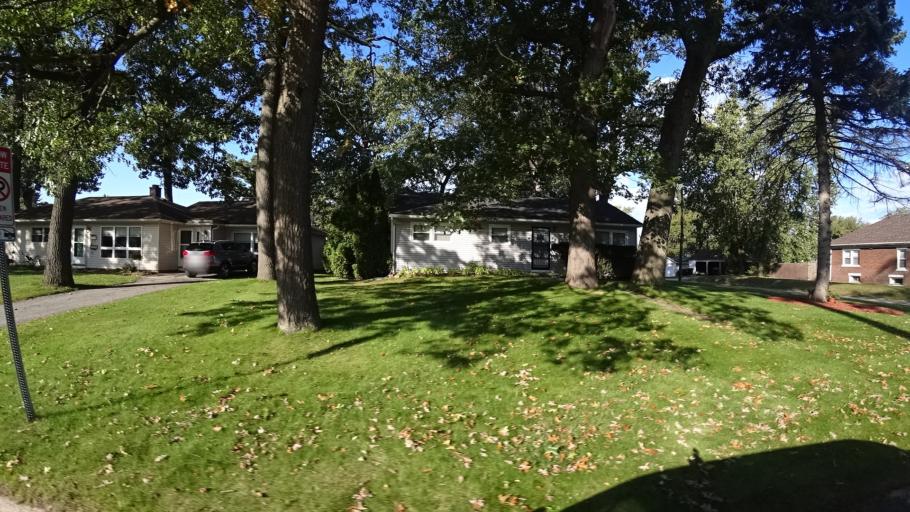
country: US
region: Indiana
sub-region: LaPorte County
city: Trail Creek
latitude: 41.7079
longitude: -86.8747
